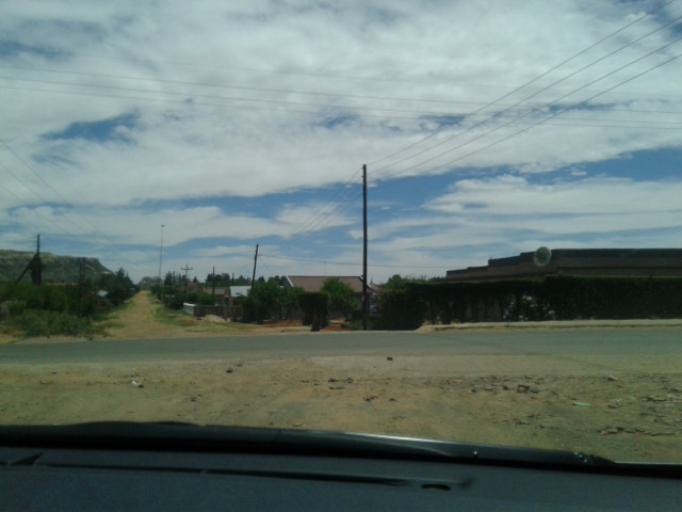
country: LS
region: Maseru
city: Maseru
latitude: -29.2954
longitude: 27.5355
